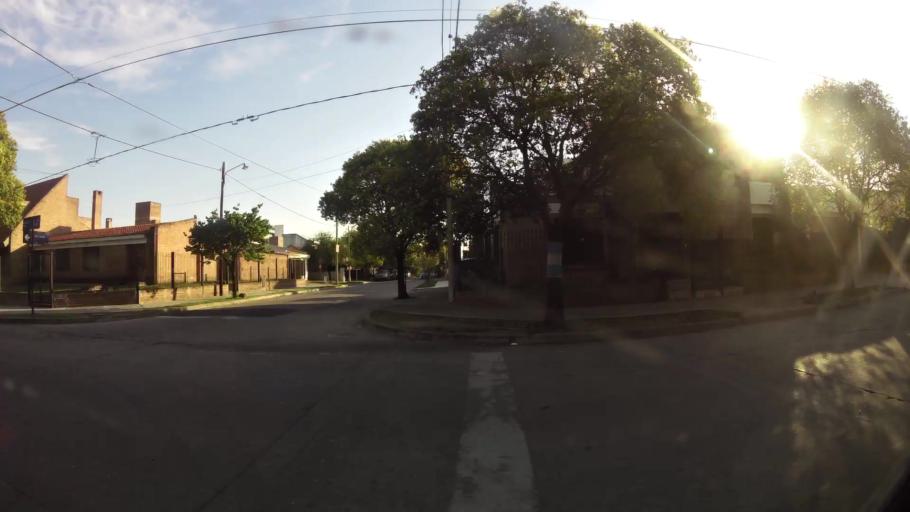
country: AR
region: Cordoba
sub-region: Departamento de Capital
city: Cordoba
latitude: -31.3808
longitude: -64.2421
